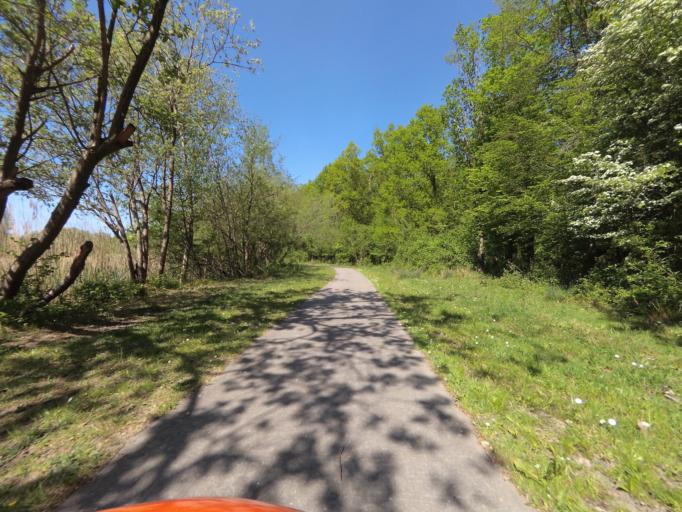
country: NL
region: Gelderland
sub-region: Gemeente Harderwijk
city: Harderwijk
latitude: 52.3890
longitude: 5.6253
